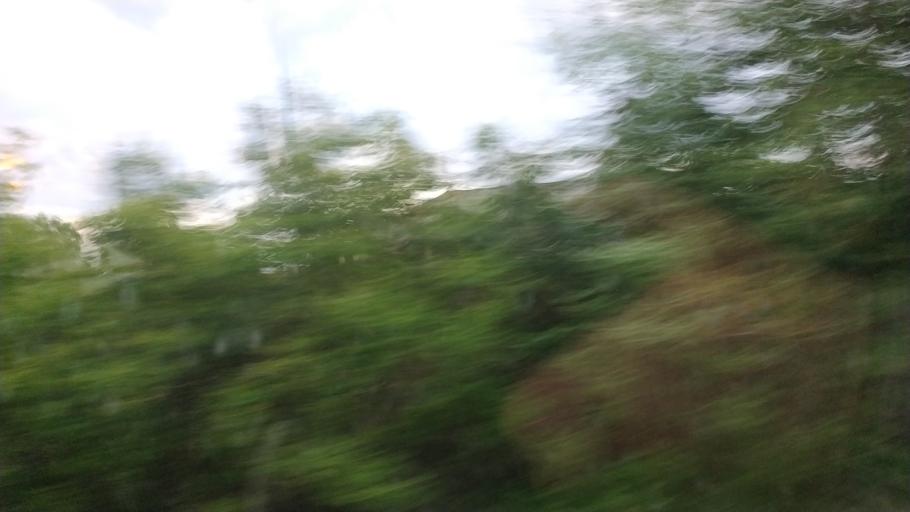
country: RU
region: Moskovskaya
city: Kashira
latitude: 54.8469
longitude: 38.1706
